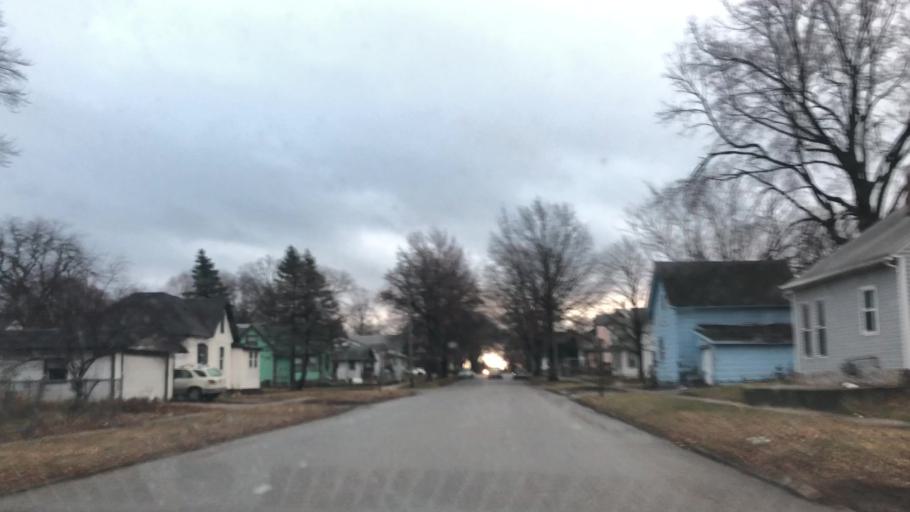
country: US
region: Iowa
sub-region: Marshall County
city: Marshalltown
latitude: 42.0544
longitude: -92.9171
